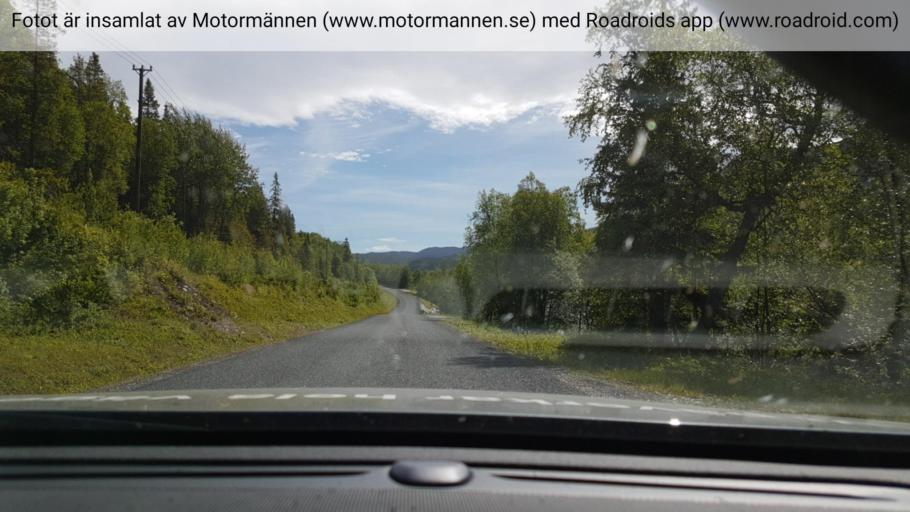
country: SE
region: Vaesterbotten
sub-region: Vilhelmina Kommun
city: Sjoberg
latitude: 65.2417
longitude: 15.4384
